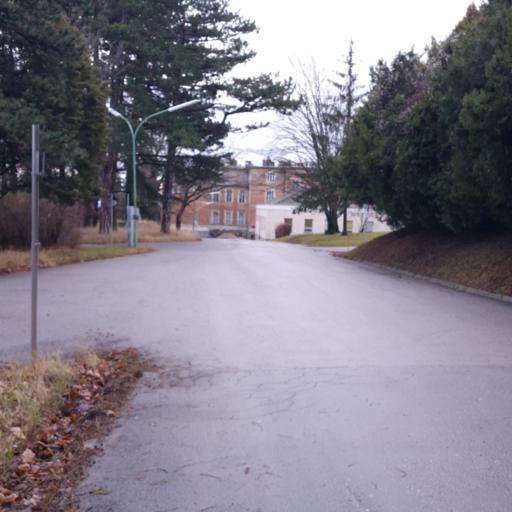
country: AT
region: Vienna
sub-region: Wien Stadt
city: Vienna
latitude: 48.2103
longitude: 16.2845
